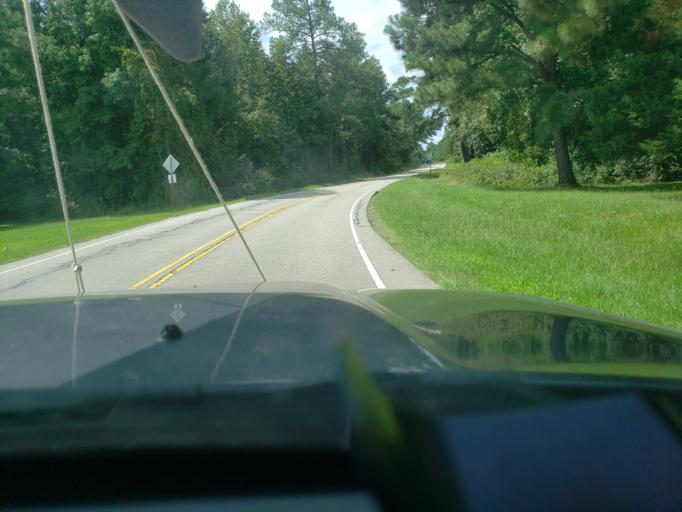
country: US
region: North Carolina
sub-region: Wake County
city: Rolesville
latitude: 35.8777
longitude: -78.4633
